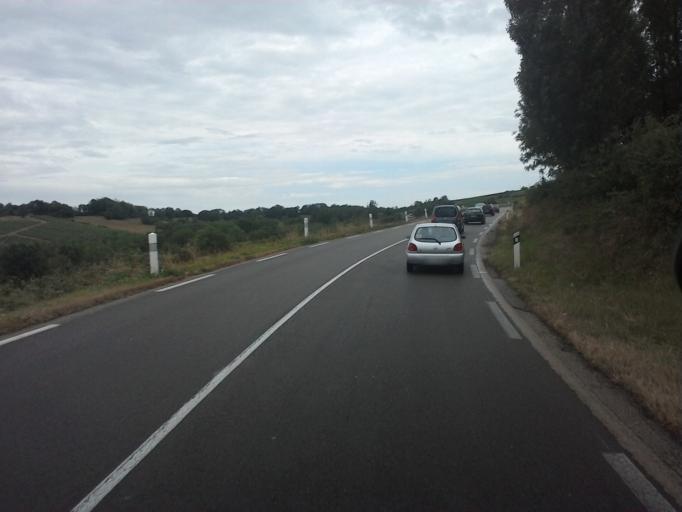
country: FR
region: Franche-Comte
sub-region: Departement du Jura
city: Poligny
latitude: 46.8830
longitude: 5.7241
